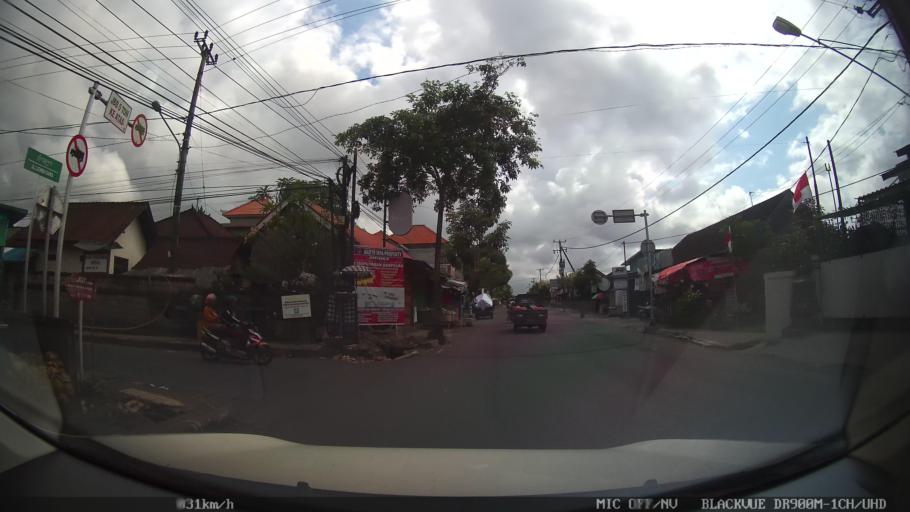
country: ID
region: Bali
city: Banjar Kertasari
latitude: -8.6207
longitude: 115.2102
